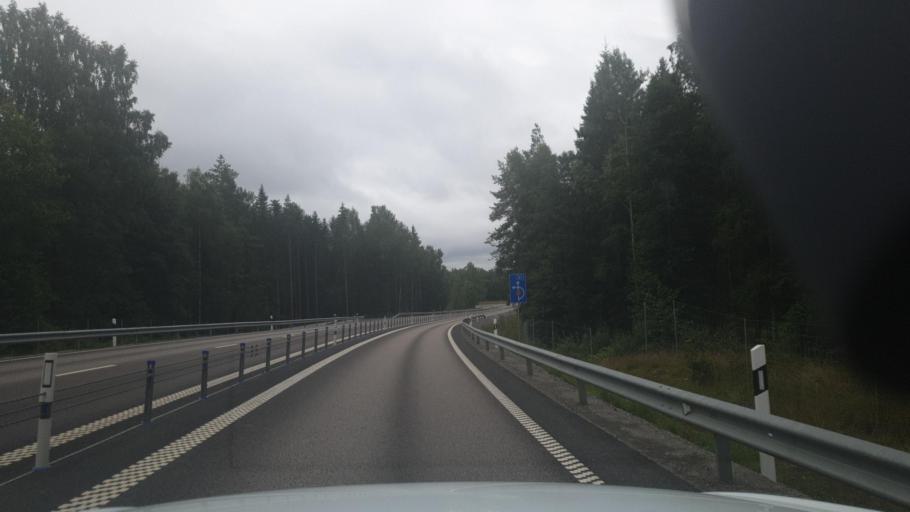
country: SE
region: Vaermland
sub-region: Arvika Kommun
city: Arvika
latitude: 59.6907
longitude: 12.5910
